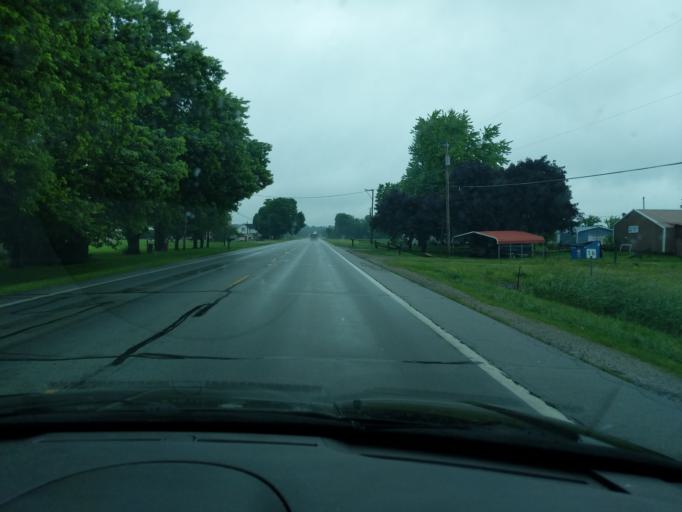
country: US
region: Ohio
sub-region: Logan County
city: West Liberty
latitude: 40.2399
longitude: -83.7524
